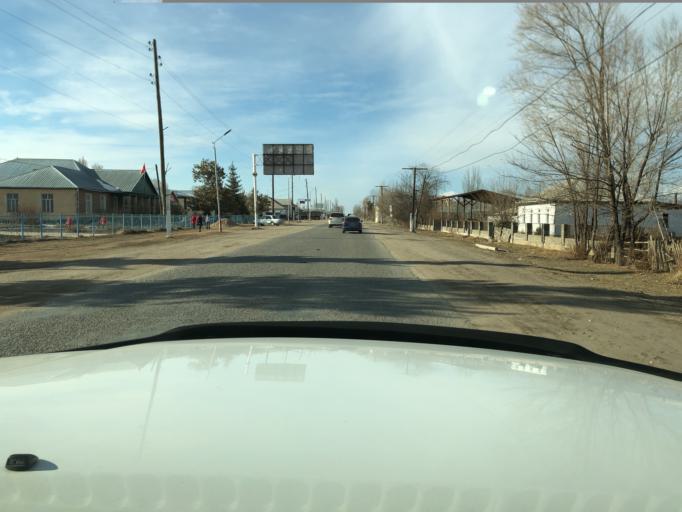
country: KG
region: Ysyk-Koel
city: Pokrovka
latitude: 42.3225
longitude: 77.9236
